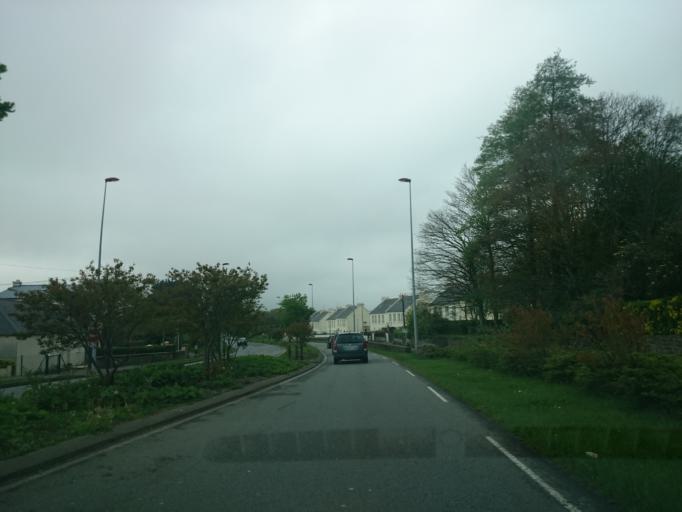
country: FR
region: Brittany
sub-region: Departement du Finistere
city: Gouesnou
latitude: 48.4432
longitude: -4.4641
